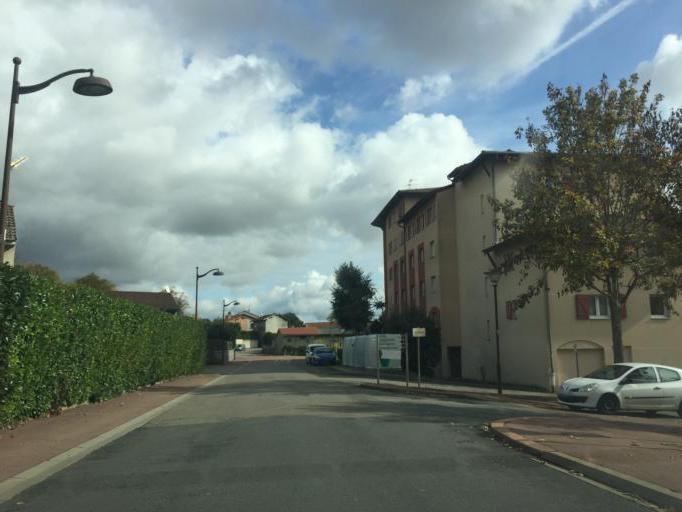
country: FR
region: Rhone-Alpes
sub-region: Departement de l'Ain
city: Dagneux
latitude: 45.8532
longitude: 5.0750
